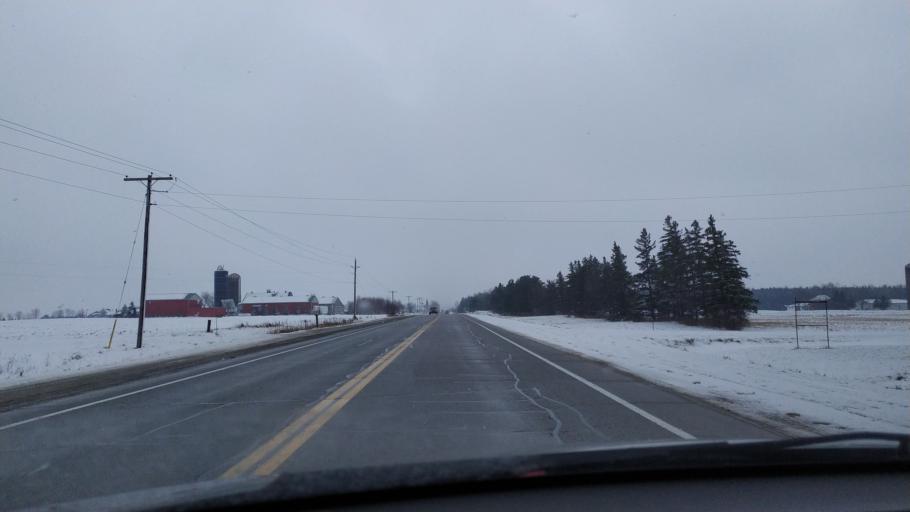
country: CA
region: Ontario
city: Waterloo
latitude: 43.6274
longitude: -80.7038
